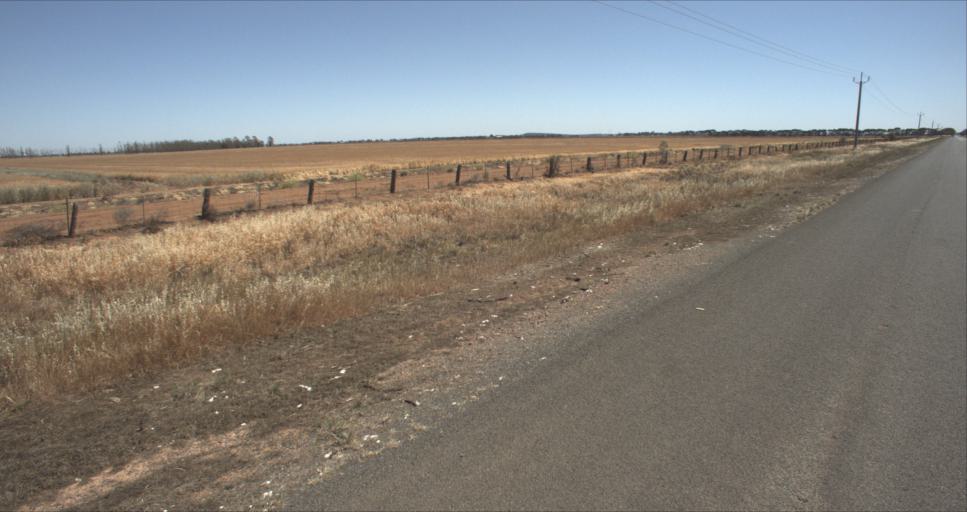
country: AU
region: New South Wales
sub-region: Leeton
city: Leeton
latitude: -34.4862
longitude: 146.2896
